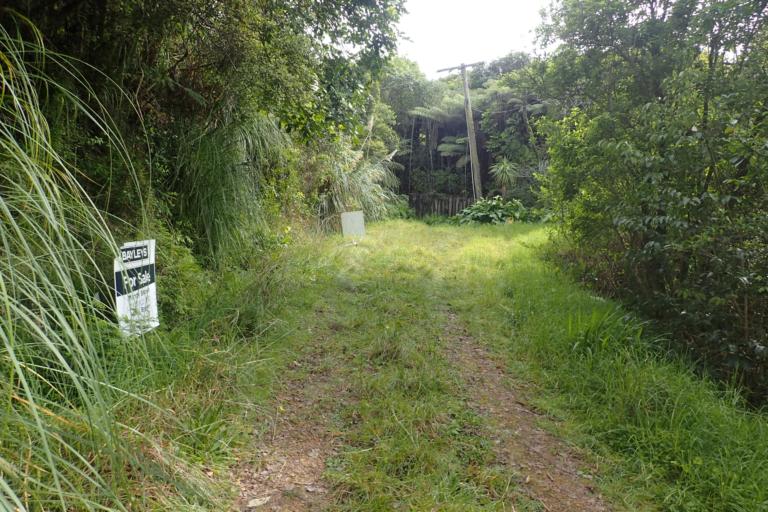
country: NZ
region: Auckland
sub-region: Auckland
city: Pakuranga
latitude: -36.7865
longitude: 175.0046
